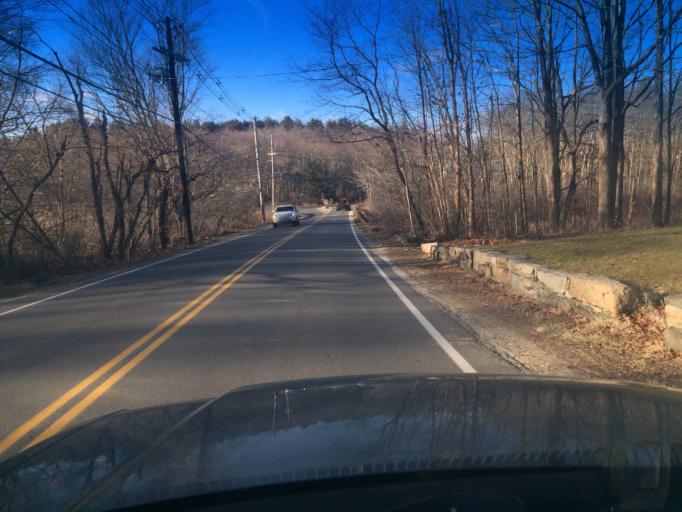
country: US
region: Massachusetts
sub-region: Middlesex County
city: Sherborn
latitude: 42.2685
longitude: -71.3814
